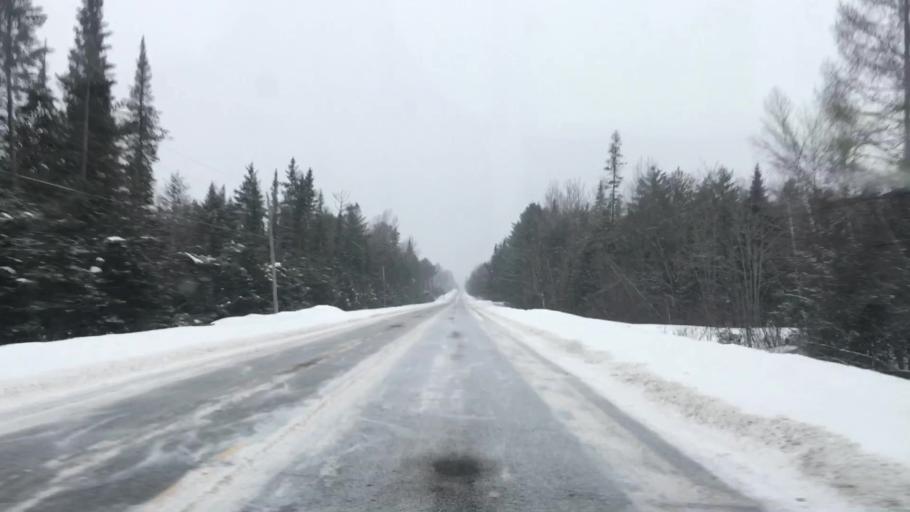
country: US
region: Maine
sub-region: Penobscot County
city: Medway
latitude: 45.5270
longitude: -68.3584
